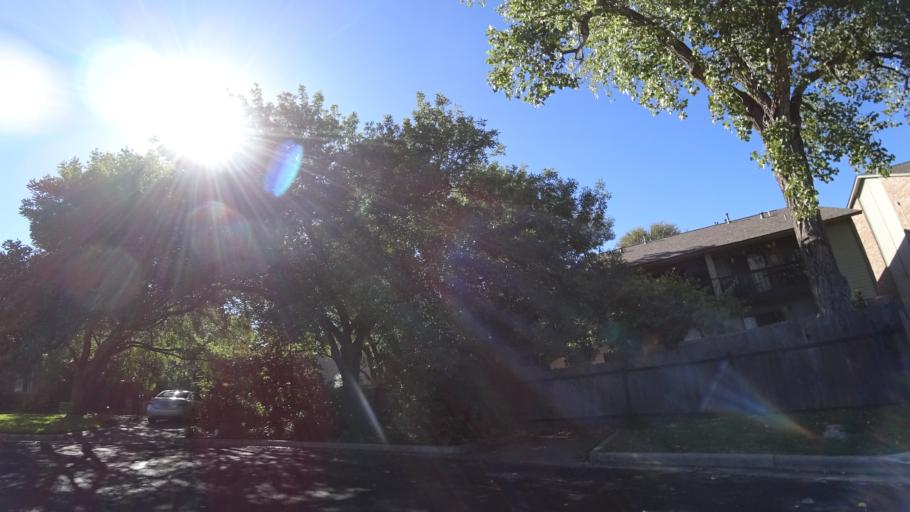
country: US
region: Texas
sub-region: Travis County
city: Rollingwood
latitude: 30.2328
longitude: -97.7884
